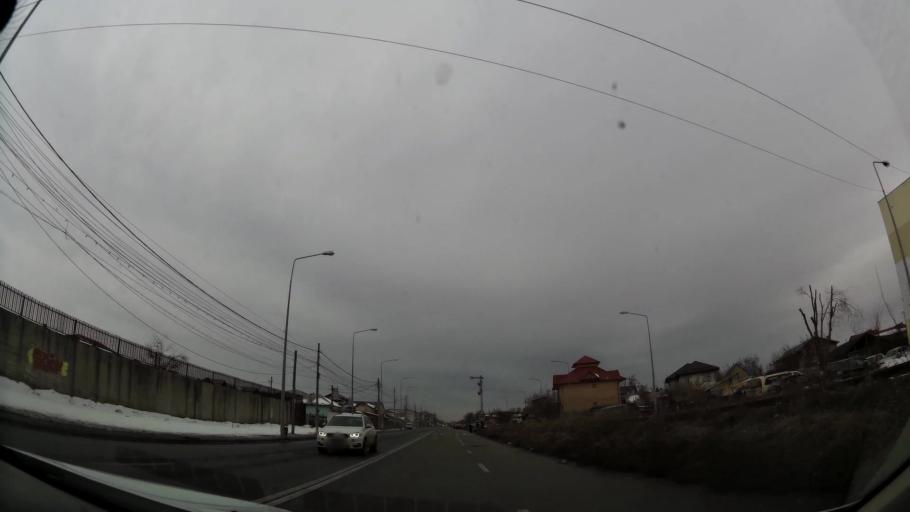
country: RO
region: Ilfov
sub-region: Comuna Glina
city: Catelu
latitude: 44.4267
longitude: 26.2171
